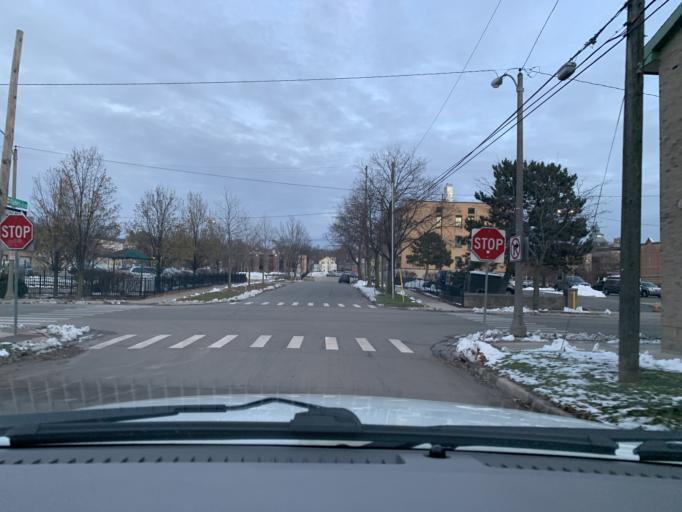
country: US
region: Michigan
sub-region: Kent County
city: Grand Rapids
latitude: 42.9609
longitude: -85.6656
